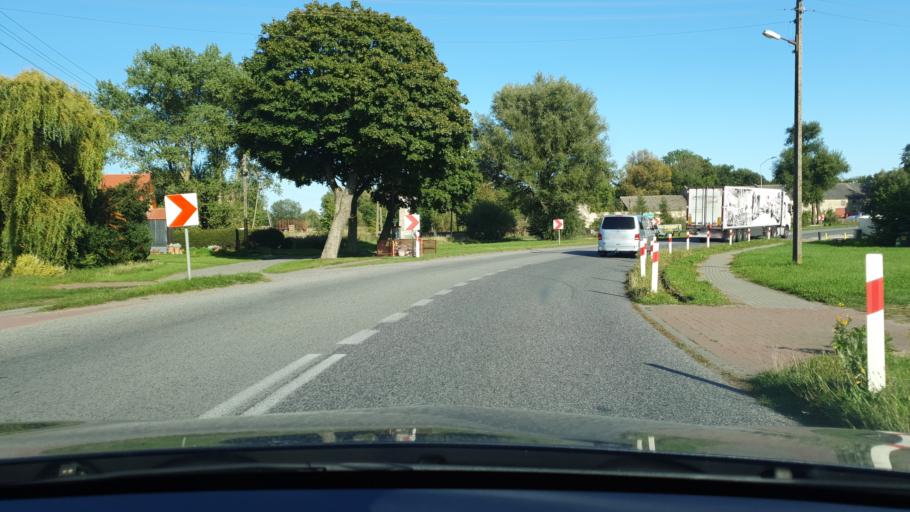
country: PL
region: West Pomeranian Voivodeship
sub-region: Powiat kamienski
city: Golczewo
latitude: 53.8324
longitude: 14.9234
